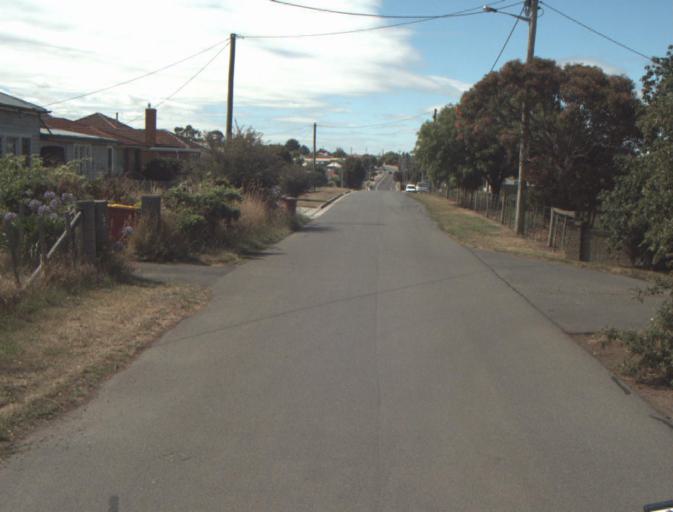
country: AU
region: Tasmania
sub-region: Launceston
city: Mayfield
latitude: -41.3820
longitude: 147.1097
